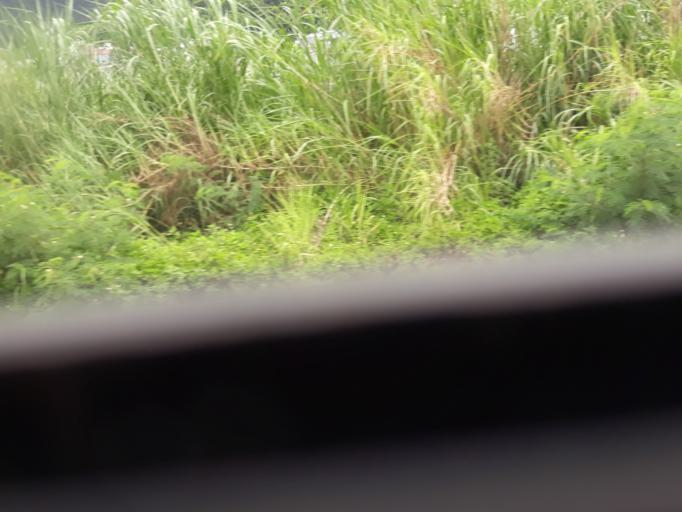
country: TW
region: Taiwan
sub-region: Yilan
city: Yilan
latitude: 24.4624
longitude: 121.8048
